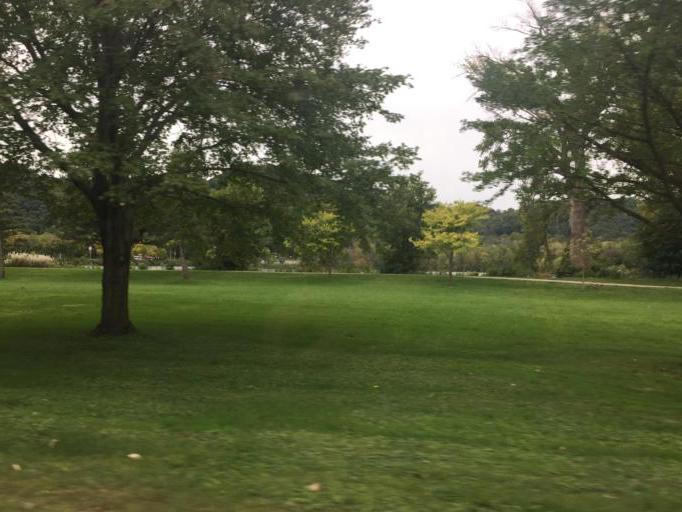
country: US
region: Minnesota
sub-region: Winona County
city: Winona
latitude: 44.0434
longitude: -91.6516
